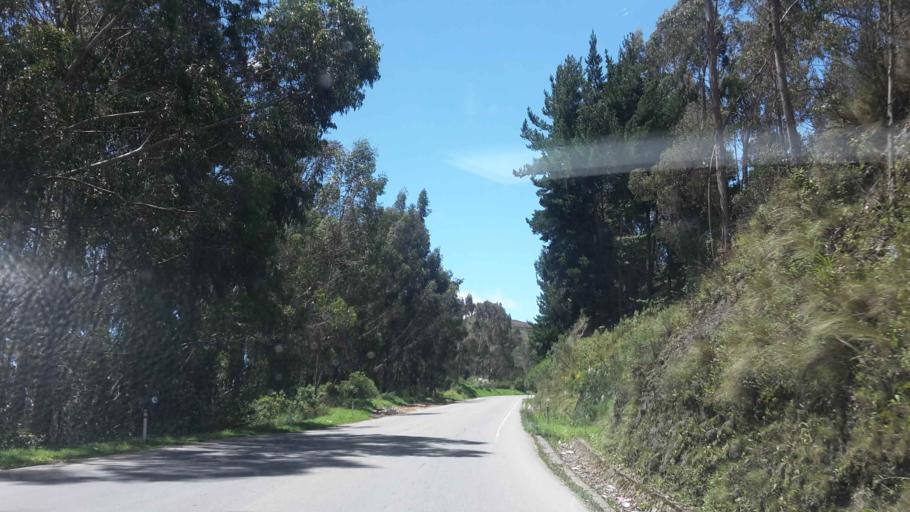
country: BO
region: Cochabamba
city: Colomi
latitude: -17.3191
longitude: -65.8736
